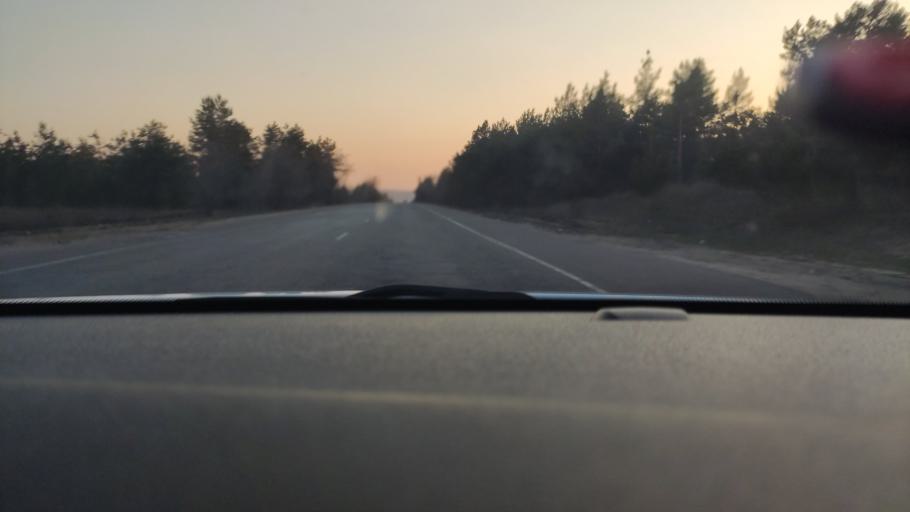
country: RU
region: Voronezj
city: Kolodeznyy
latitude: 51.3649
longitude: 39.1939
